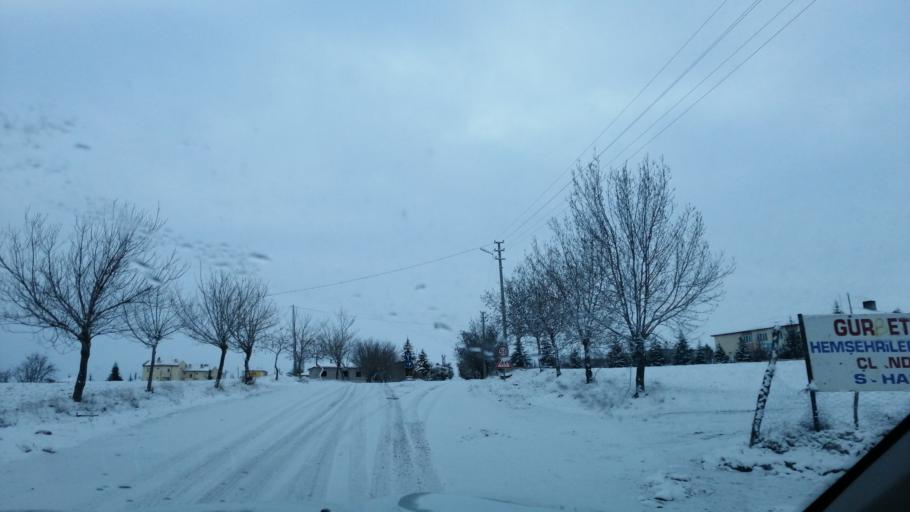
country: TR
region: Aksaray
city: Agacoren
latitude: 38.9300
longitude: 33.9530
